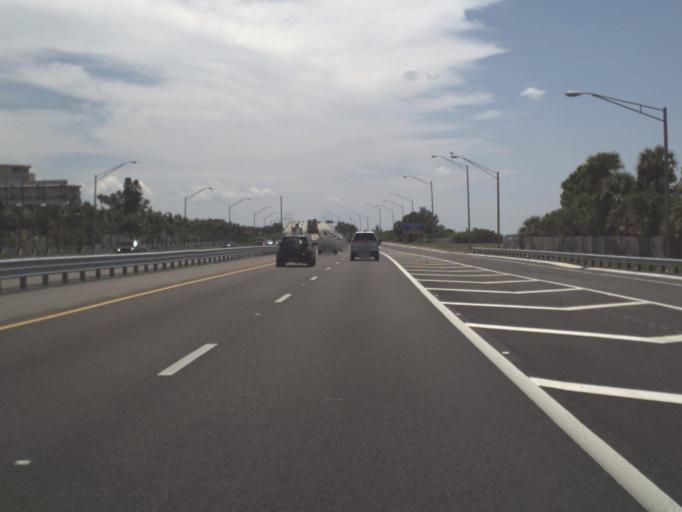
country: US
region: Florida
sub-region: Pinellas County
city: Tierra Verde
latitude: 27.7032
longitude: -82.6794
